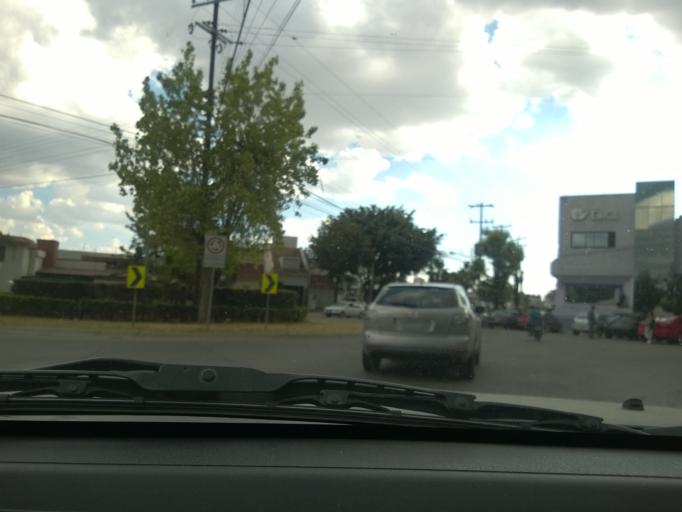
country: MX
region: Guanajuato
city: Leon
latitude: 21.1405
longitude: -101.6922
